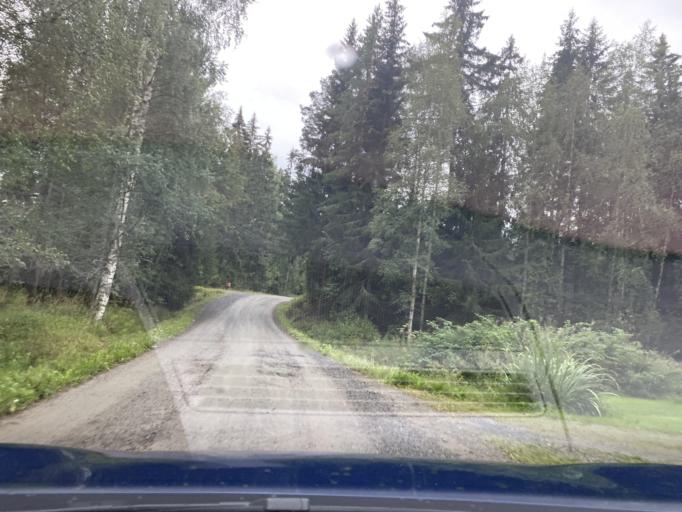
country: FI
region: Pirkanmaa
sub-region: Lounais-Pirkanmaa
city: Punkalaidun
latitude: 61.2220
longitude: 23.0365
